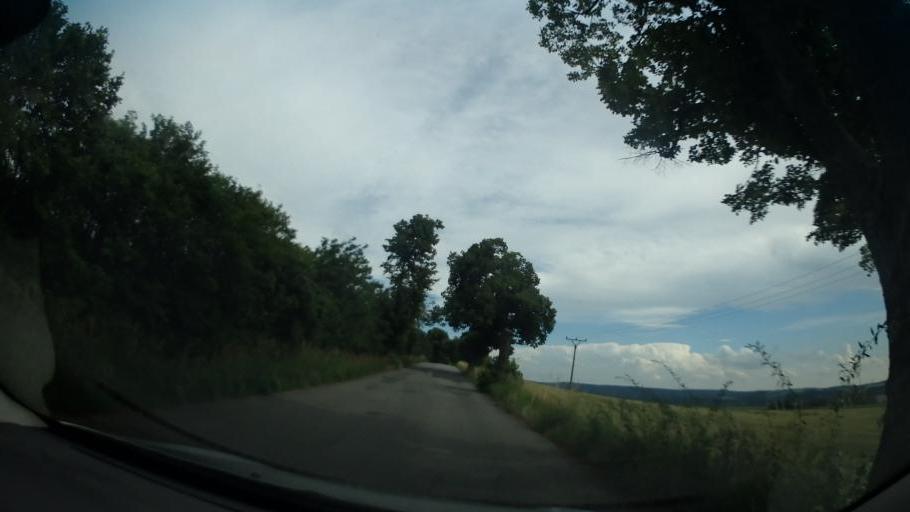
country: CZ
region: South Moravian
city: Oslavany
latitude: 49.1271
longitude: 16.3604
